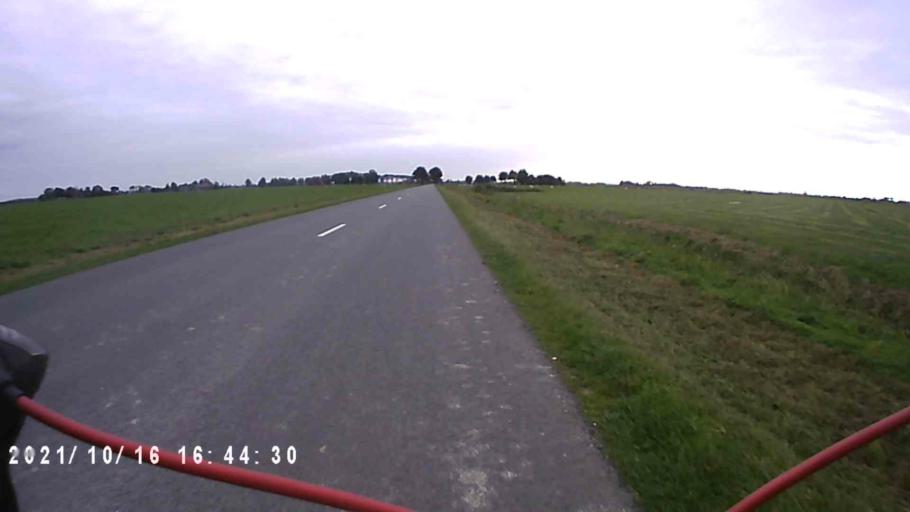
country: NL
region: Friesland
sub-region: Gemeente Dongeradeel
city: Anjum
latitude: 53.3679
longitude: 6.1422
